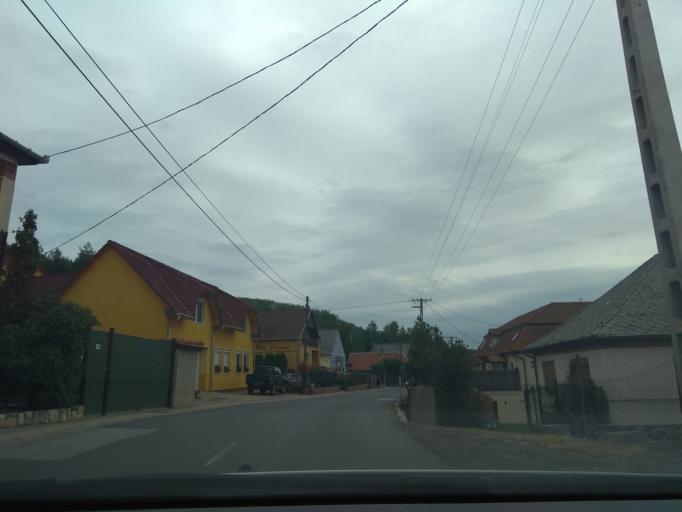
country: HU
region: Heves
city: Egerszalok
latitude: 47.8692
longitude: 20.3249
